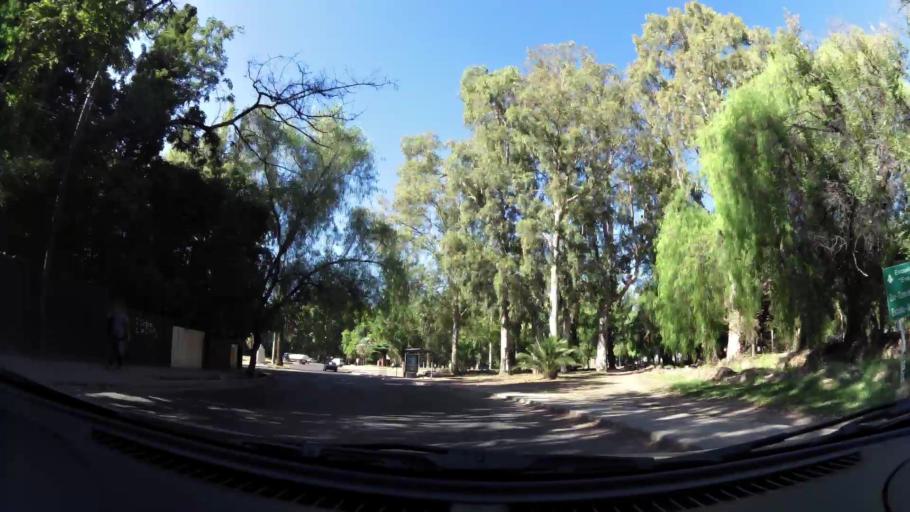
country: AR
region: Mendoza
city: Mendoza
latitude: -32.8837
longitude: -68.8737
